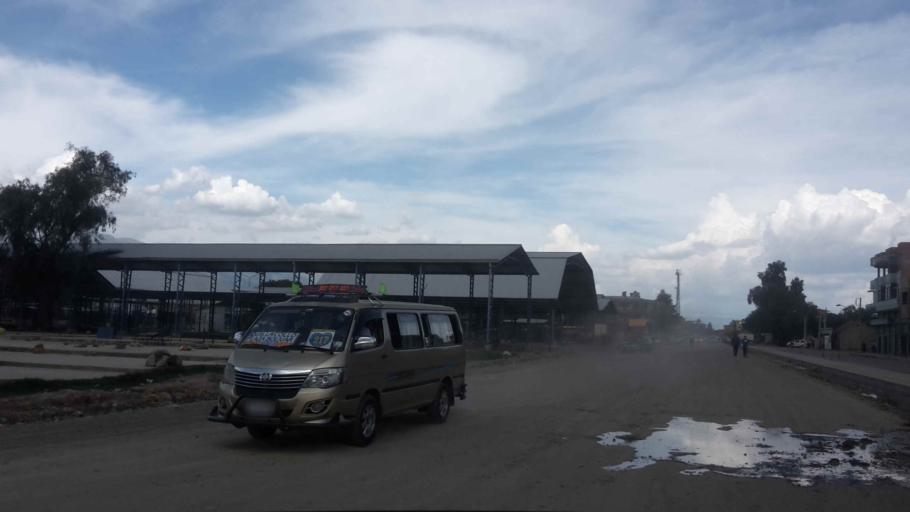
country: BO
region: Cochabamba
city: Sipe Sipe
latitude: -17.4019
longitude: -66.2862
